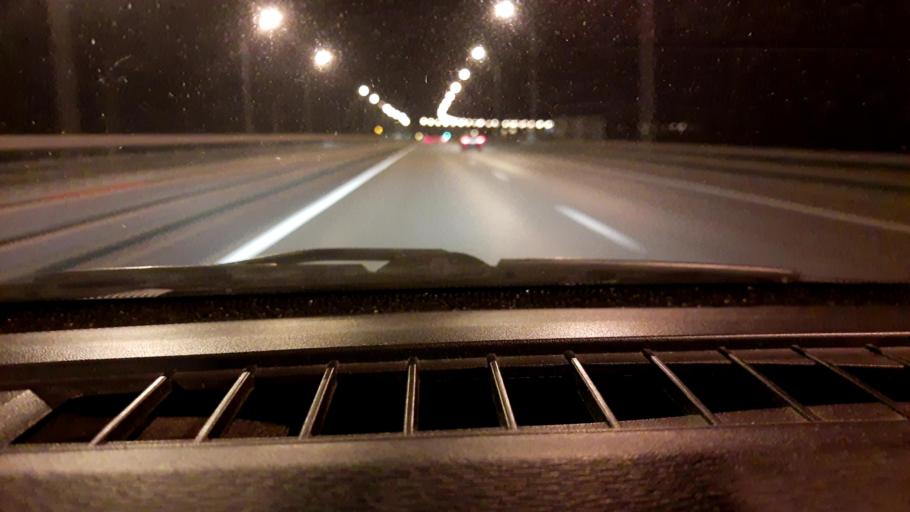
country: RU
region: Nizjnij Novgorod
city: Neklyudovo
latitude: 56.3876
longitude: 43.9690
